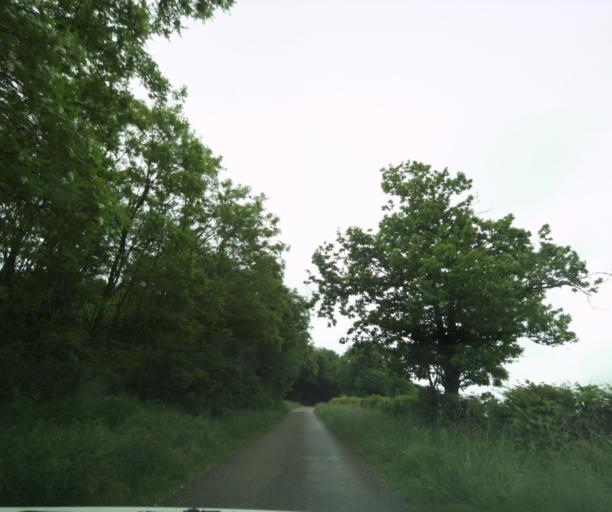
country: FR
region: Bourgogne
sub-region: Departement de Saone-et-Loire
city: Charolles
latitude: 46.4997
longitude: 4.2850
